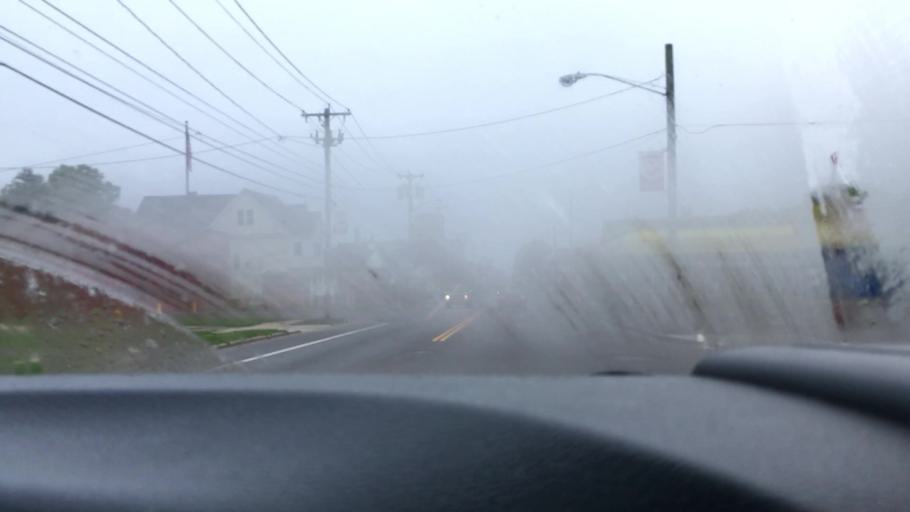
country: US
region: New York
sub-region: Onondaga County
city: Syracuse
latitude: 43.0231
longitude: -76.1441
